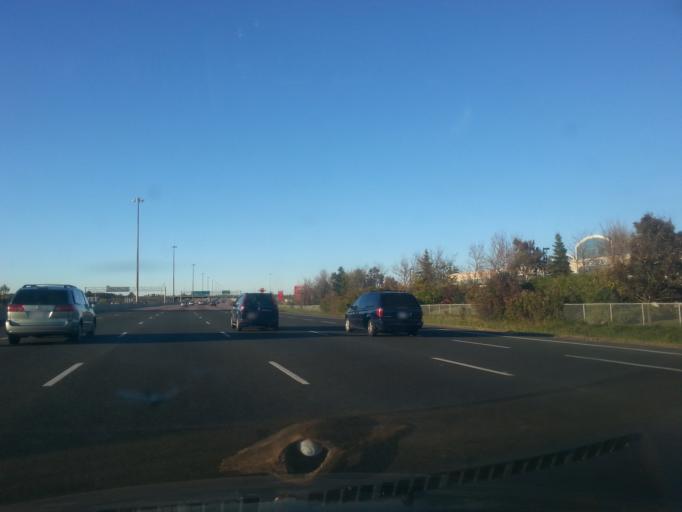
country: CA
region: Ontario
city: Vaughan
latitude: 43.8136
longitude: -79.5445
